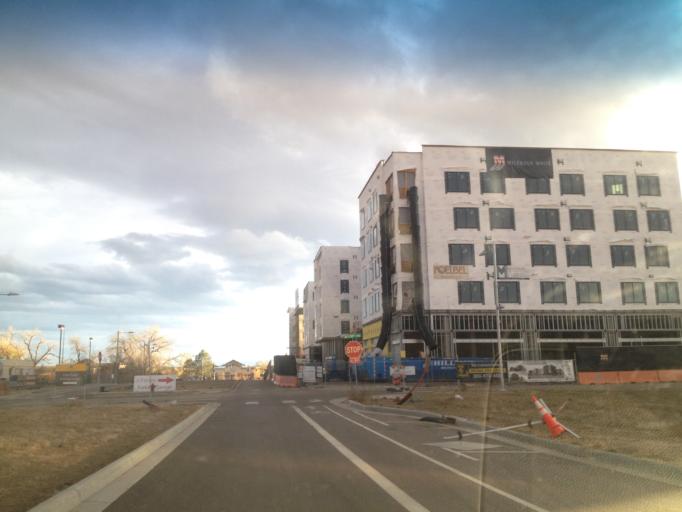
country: US
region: Colorado
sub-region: Adams County
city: Westminster
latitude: 39.8590
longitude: -105.0583
